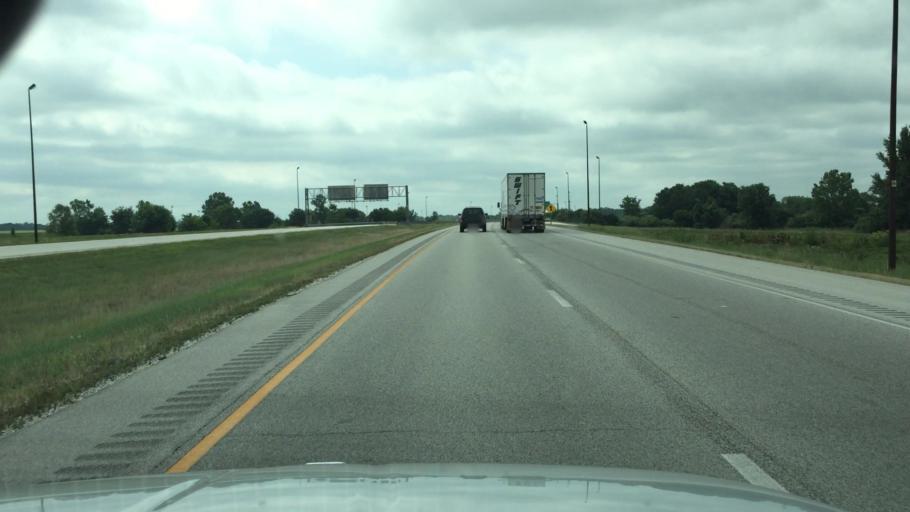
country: US
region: Illinois
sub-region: Henry County
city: Green Rock
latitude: 41.4430
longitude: -90.3310
